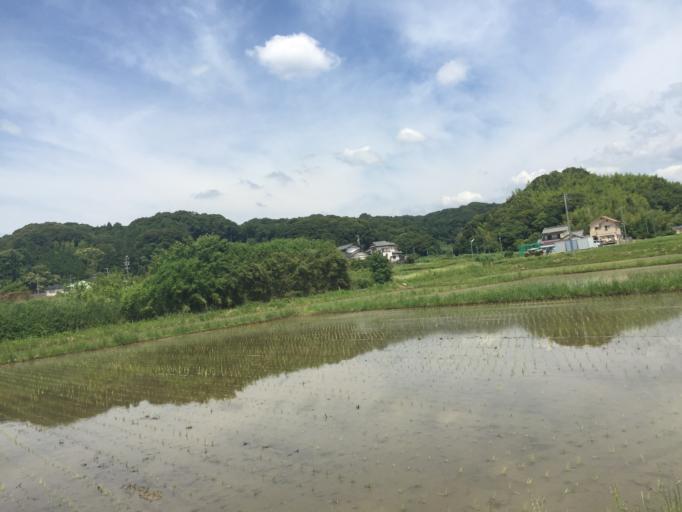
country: JP
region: Shizuoka
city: Mori
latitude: 34.8109
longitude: 137.9493
